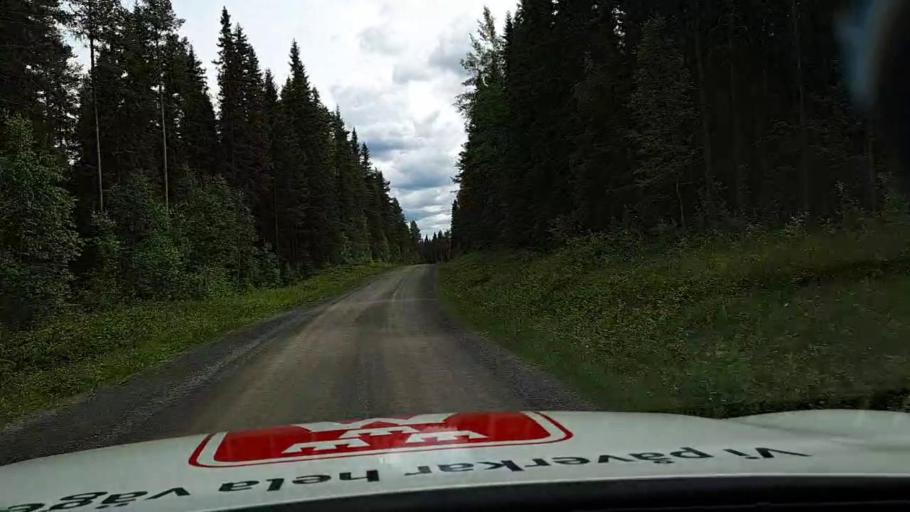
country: SE
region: Jaemtland
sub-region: Braecke Kommun
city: Braecke
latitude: 63.2777
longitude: 15.3719
